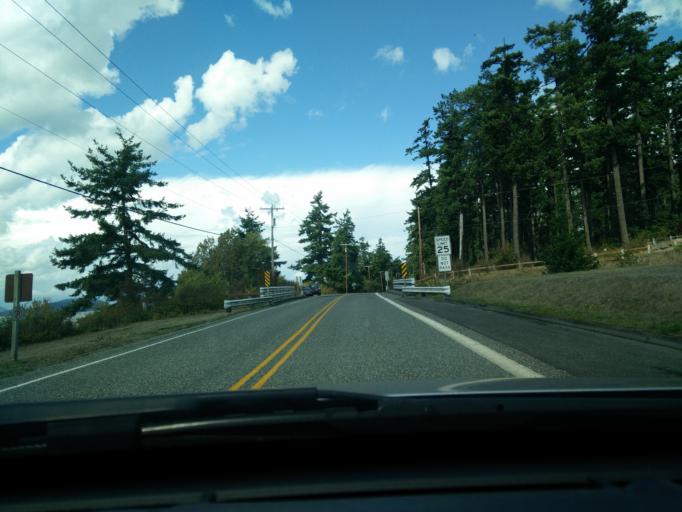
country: US
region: Washington
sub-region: Skagit County
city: Anacortes
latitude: 48.4877
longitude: -122.4803
